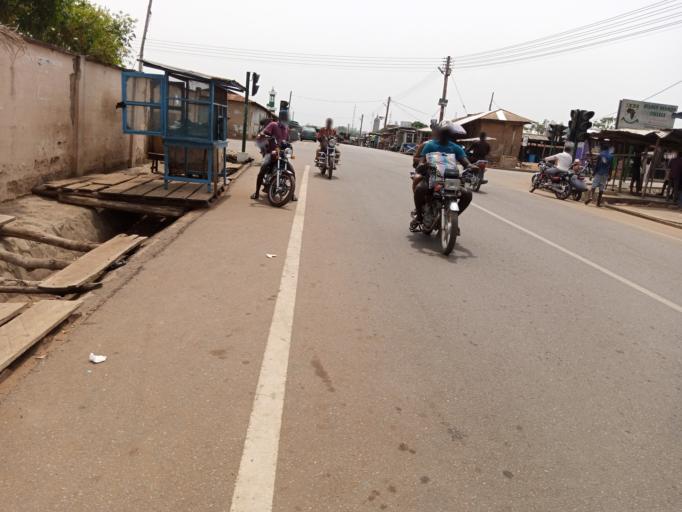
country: GH
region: Volta
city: Kpandu
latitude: 7.0027
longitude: 0.2953
